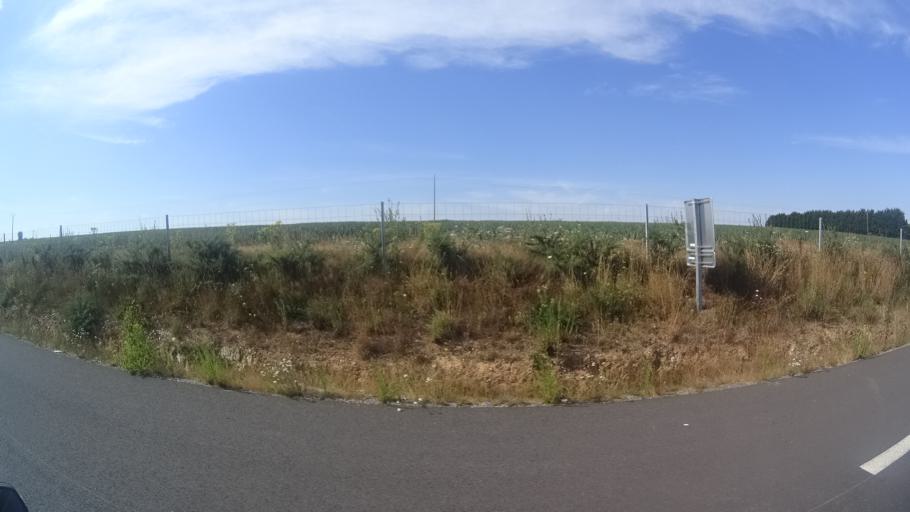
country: FR
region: Brittany
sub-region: Departement du Morbihan
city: Saint-Jean-la-Poterie
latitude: 47.6133
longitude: -2.1374
